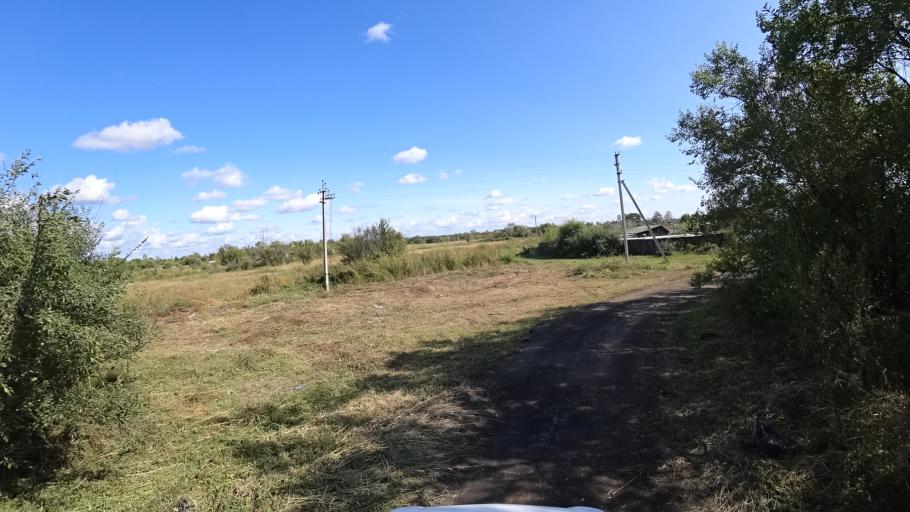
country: RU
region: Amur
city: Arkhara
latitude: 49.4045
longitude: 130.1413
